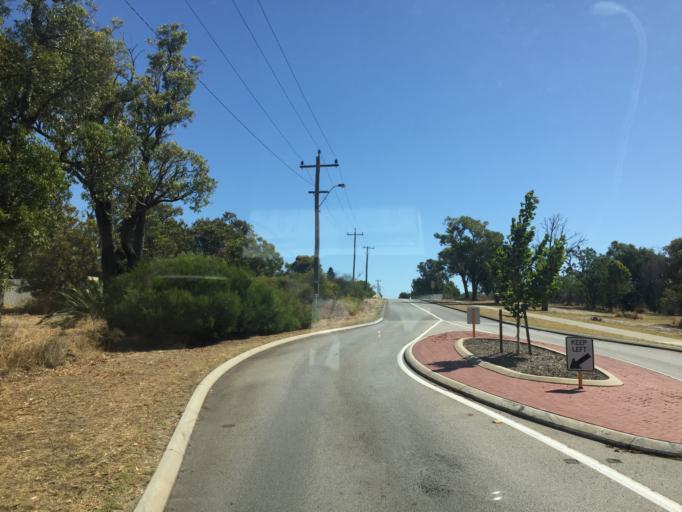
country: AU
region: Western Australia
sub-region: Belmont
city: Redcliffe
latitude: -31.9359
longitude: 115.9464
